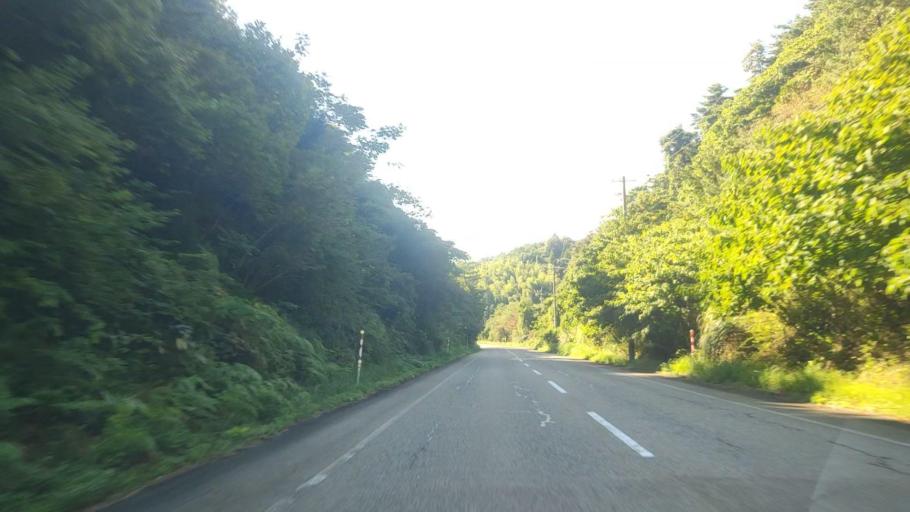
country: JP
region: Ishikawa
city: Nanao
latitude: 37.3147
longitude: 137.1544
